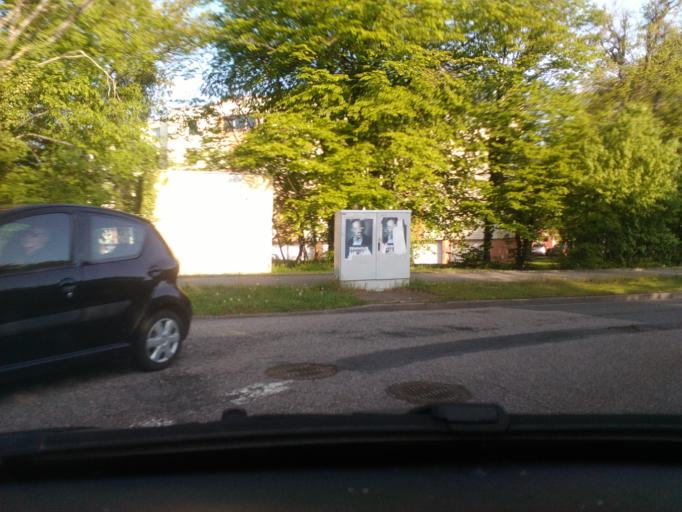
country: FR
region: Lorraine
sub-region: Departement de Meurthe-et-Moselle
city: Vandoeuvre-les-Nancy
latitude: 48.6486
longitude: 6.1601
